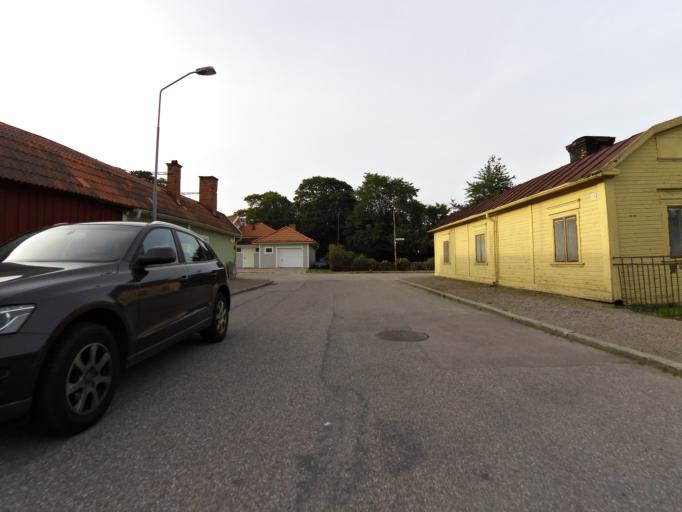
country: SE
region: Gaevleborg
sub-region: Gavle Kommun
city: Gavle
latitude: 60.7024
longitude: 17.1602
